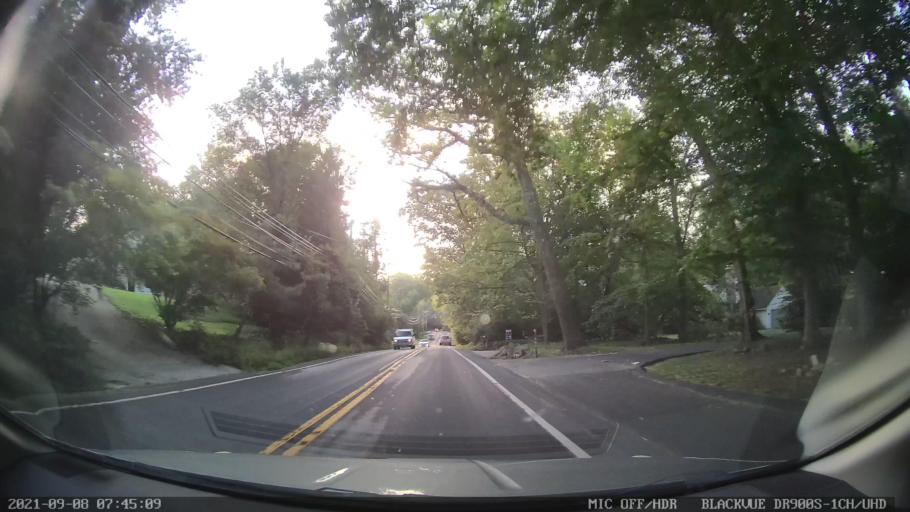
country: US
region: Pennsylvania
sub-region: Delaware County
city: Radnor
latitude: 40.0583
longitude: -75.3710
